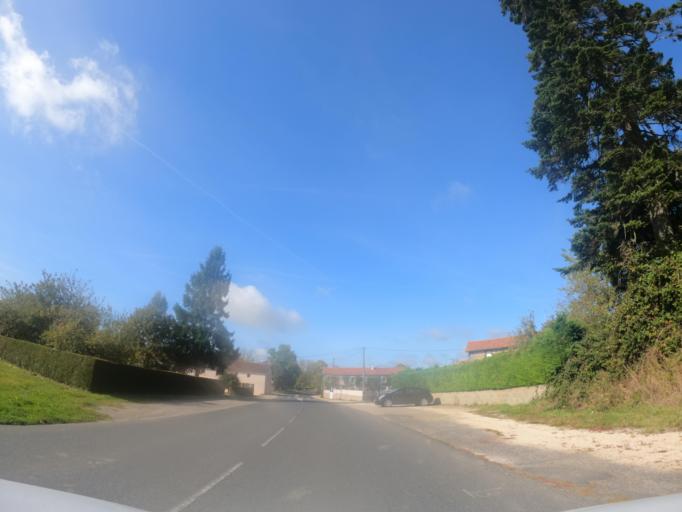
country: FR
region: Poitou-Charentes
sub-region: Departement des Deux-Sevres
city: Courlay
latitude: 46.7858
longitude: -0.5725
